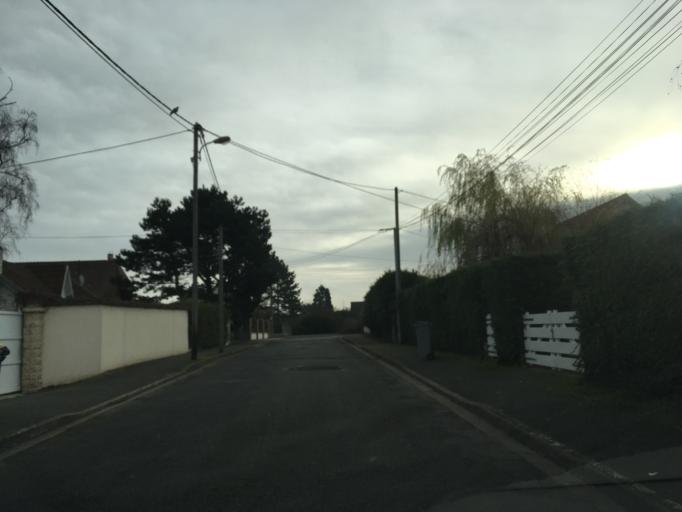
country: FR
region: Haute-Normandie
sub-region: Departement de l'Eure
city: Vernon
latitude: 49.0852
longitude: 1.4894
